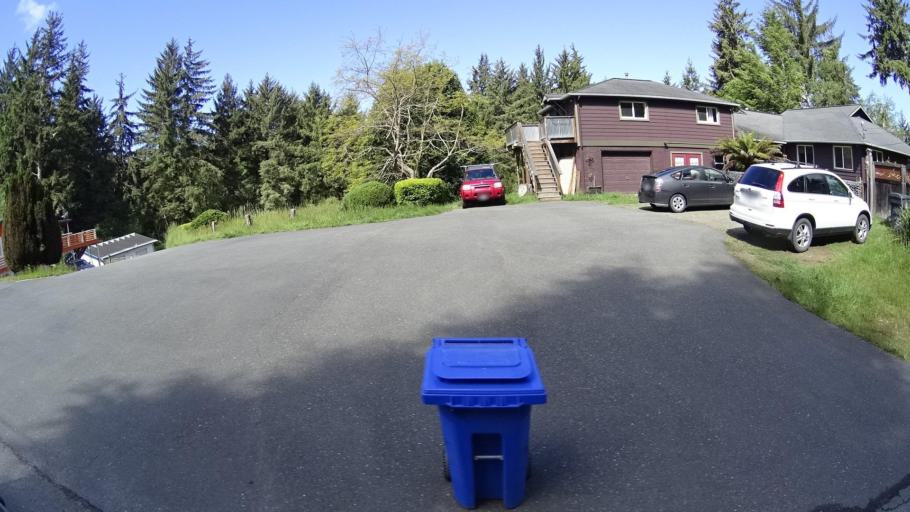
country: US
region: California
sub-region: Humboldt County
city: McKinleyville
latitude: 40.9301
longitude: -124.0816
